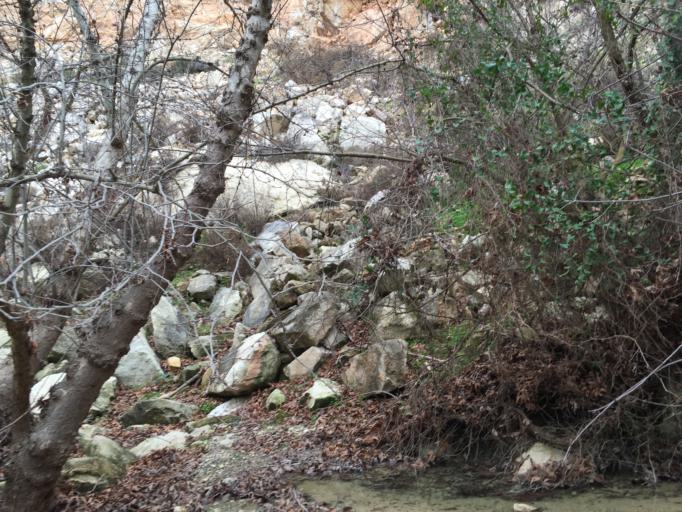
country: CY
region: Pafos
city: Pegeia
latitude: 34.9269
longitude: 32.3572
